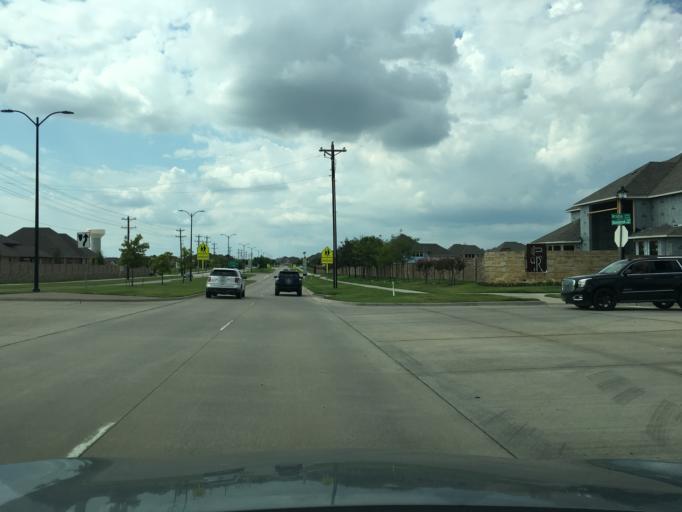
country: US
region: Texas
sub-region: Denton County
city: The Colony
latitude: 33.1376
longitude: -96.8787
